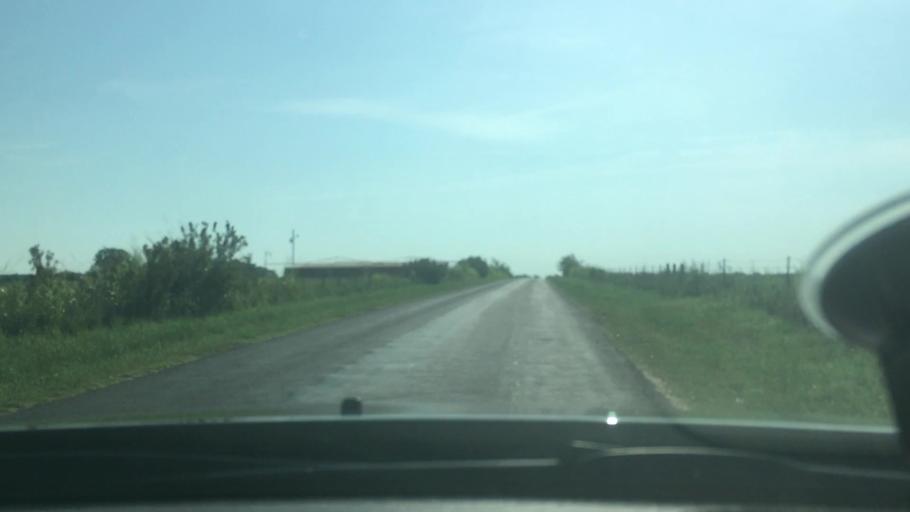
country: US
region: Oklahoma
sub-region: Garvin County
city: Maysville
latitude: 34.6520
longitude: -97.4049
